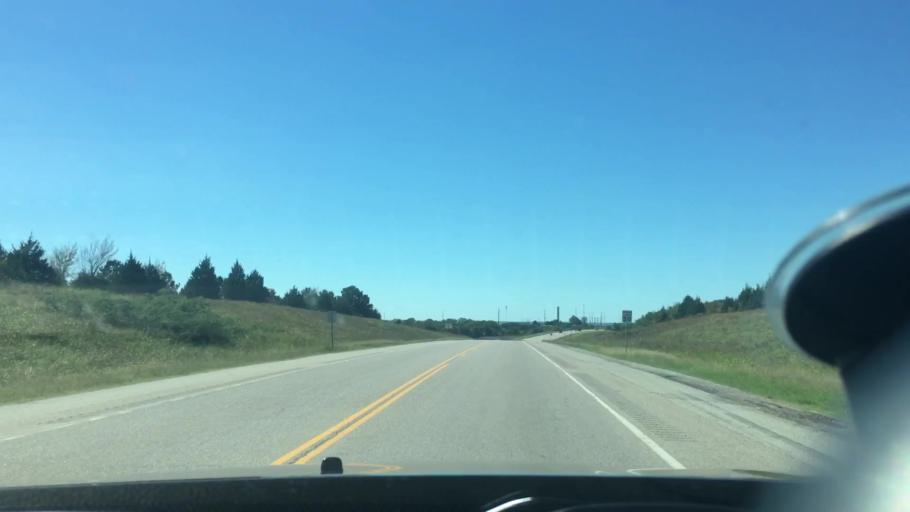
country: US
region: Oklahoma
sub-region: Coal County
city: Coalgate
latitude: 34.6110
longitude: -96.4251
